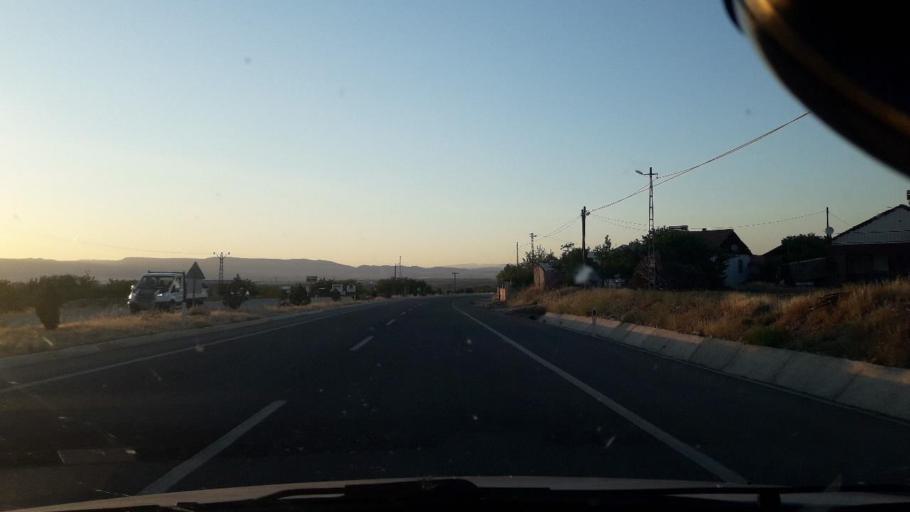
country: TR
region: Malatya
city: Yazihan
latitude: 38.4849
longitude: 38.2173
